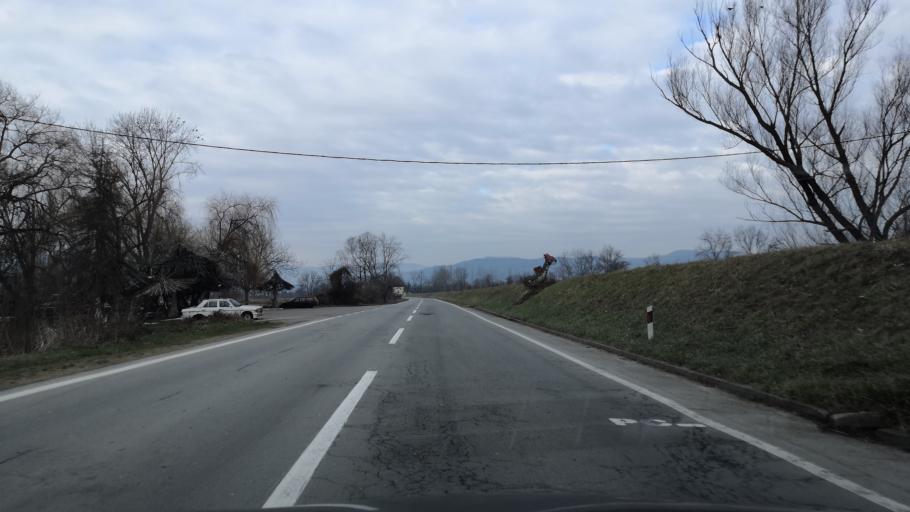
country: BA
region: Republika Srpska
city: Petkovci
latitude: 44.5208
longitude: 19.1509
